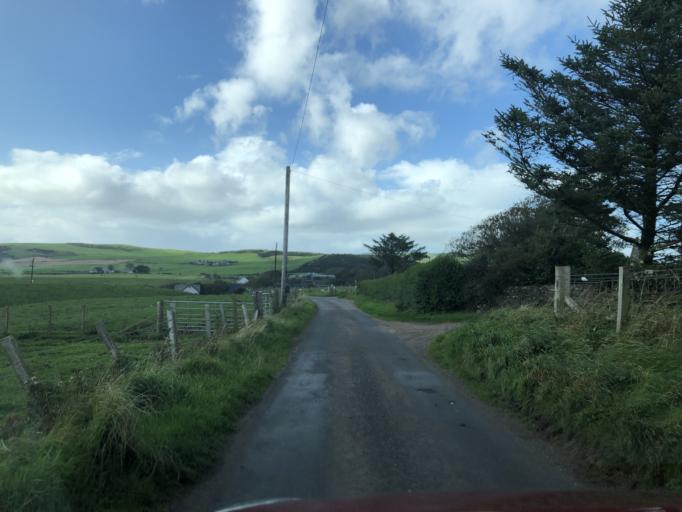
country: GB
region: Scotland
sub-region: Argyll and Bute
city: Campbeltown
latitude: 55.3219
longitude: -5.6202
